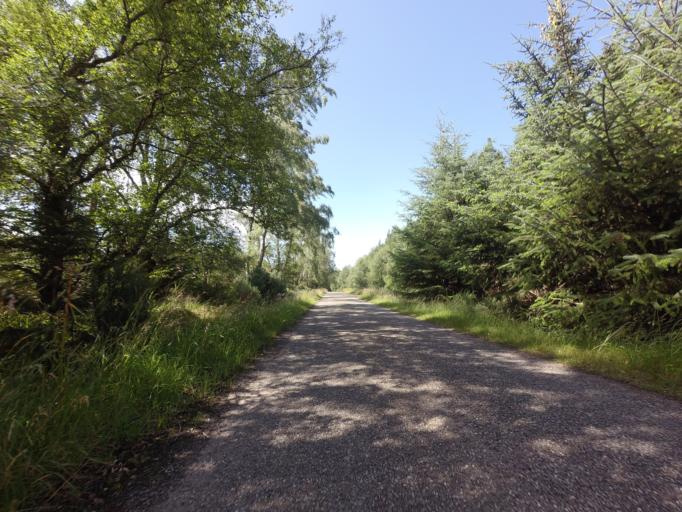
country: GB
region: Scotland
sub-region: Highland
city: Nairn
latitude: 57.5035
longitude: -3.9191
